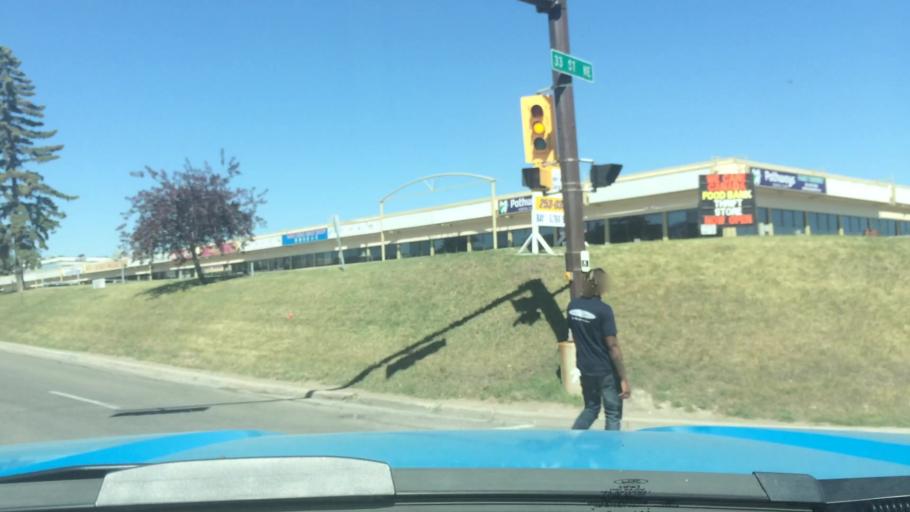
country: CA
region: Alberta
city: Calgary
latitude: 51.0571
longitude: -113.9861
